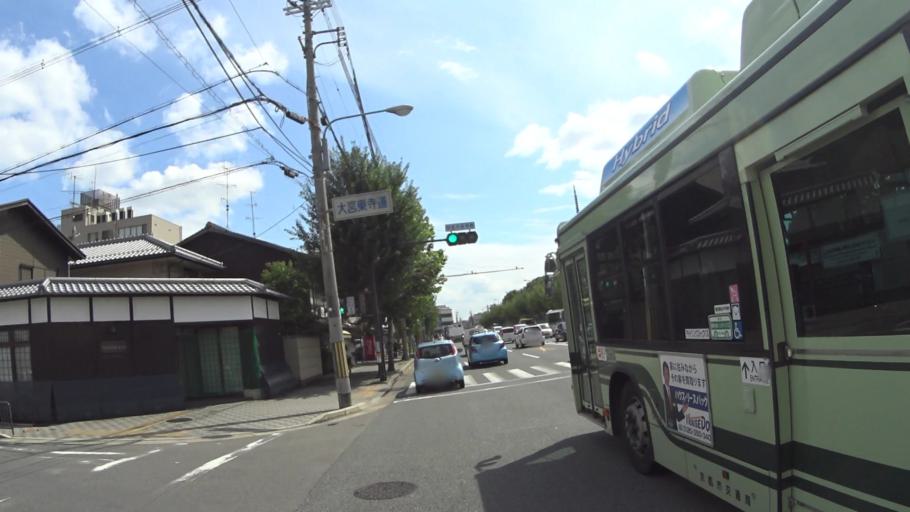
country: JP
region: Kyoto
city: Kyoto
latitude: 34.9821
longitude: 135.7493
